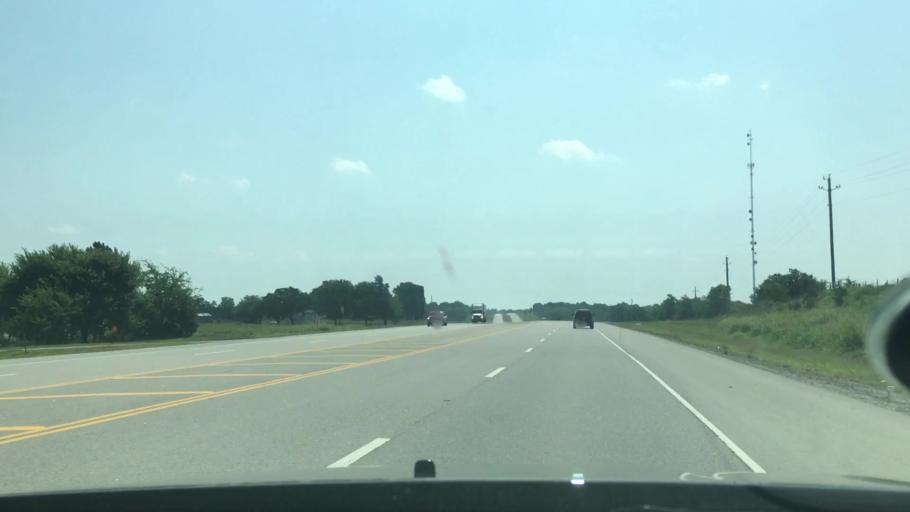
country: US
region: Oklahoma
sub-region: Atoka County
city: Atoka
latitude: 34.3590
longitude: -96.0942
